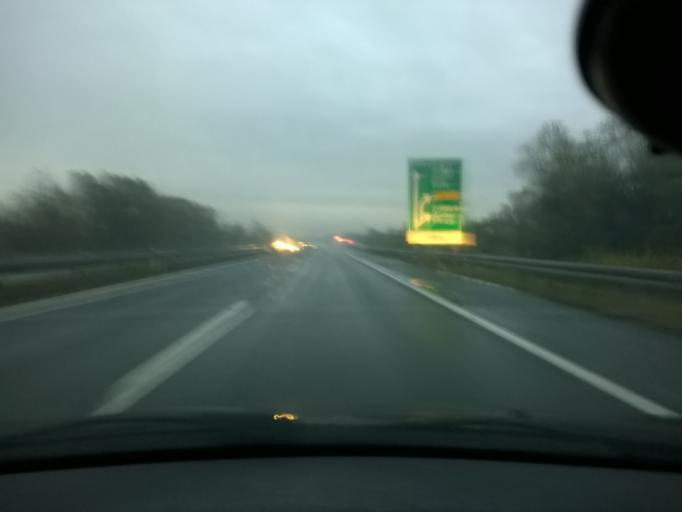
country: HR
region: Zagrebacka
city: Rakitje
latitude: 45.8010
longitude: 15.8399
